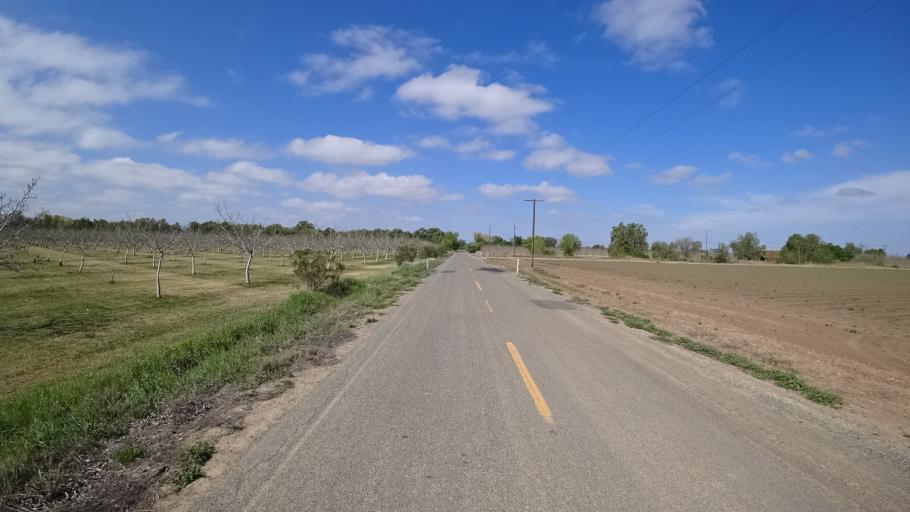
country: US
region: California
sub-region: Colusa County
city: Colusa
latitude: 39.4199
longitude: -121.9573
